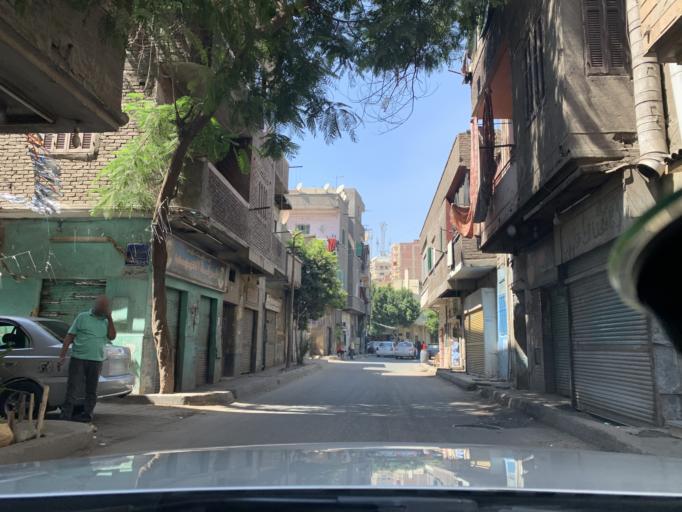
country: EG
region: Muhafazat al Qahirah
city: Cairo
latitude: 30.0711
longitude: 31.2559
